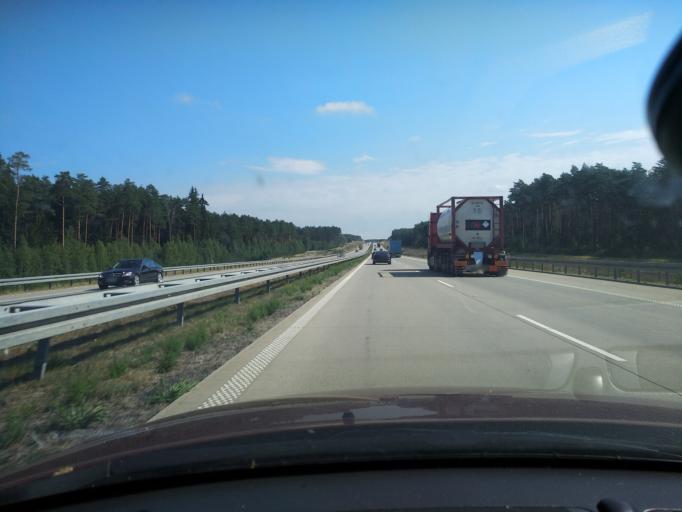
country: PL
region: Lower Silesian Voivodeship
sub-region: Powiat boleslawiecki
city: Nowogrodziec
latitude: 51.2738
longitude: 15.4452
